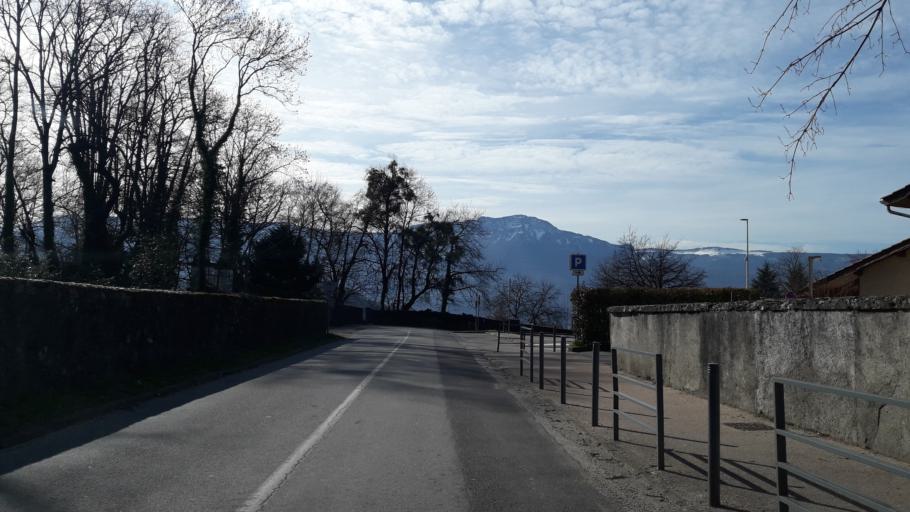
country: FR
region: Rhone-Alpes
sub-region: Departement de l'Isere
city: Herbeys
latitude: 45.1398
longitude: 5.7921
